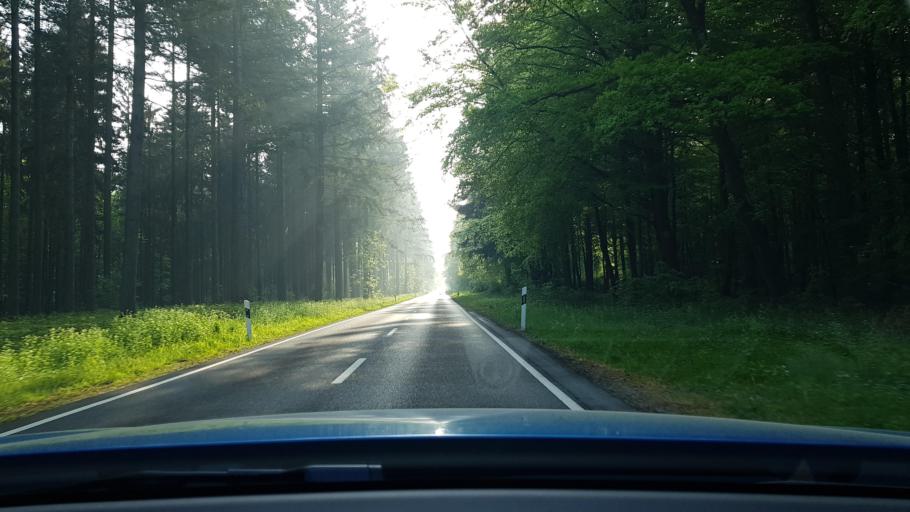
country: LU
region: Luxembourg
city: Helmsange
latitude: 49.6586
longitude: 6.1772
